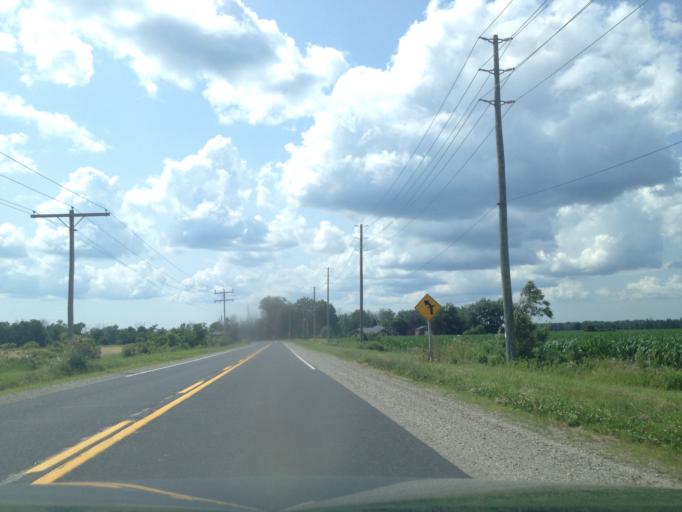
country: CA
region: Ontario
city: Aylmer
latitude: 42.6730
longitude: -80.8564
